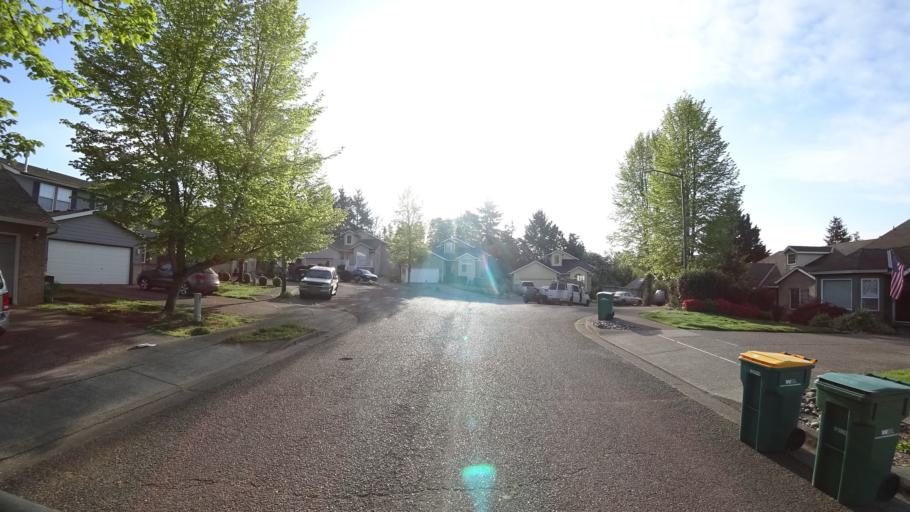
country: US
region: Oregon
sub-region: Washington County
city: Beaverton
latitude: 45.4454
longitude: -122.8244
